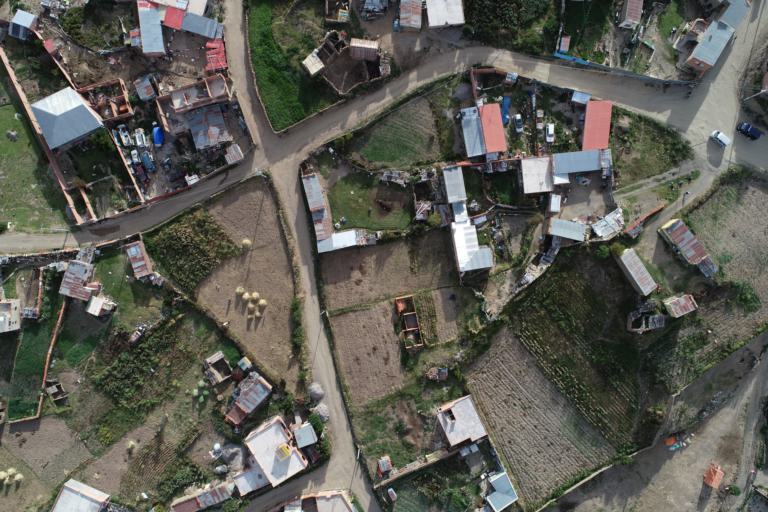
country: BO
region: La Paz
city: La Paz
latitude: -16.5453
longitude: -67.9999
